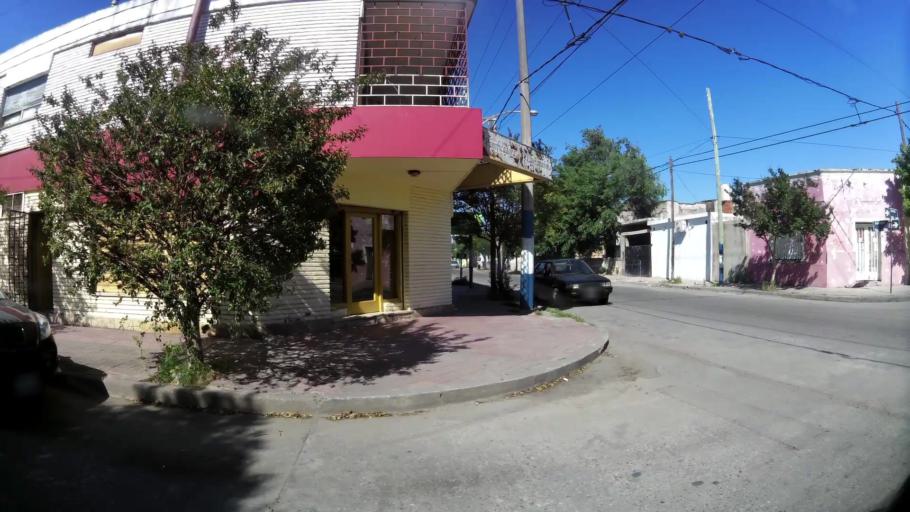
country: AR
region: Cordoba
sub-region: Departamento de Capital
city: Cordoba
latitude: -31.4377
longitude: -64.1561
